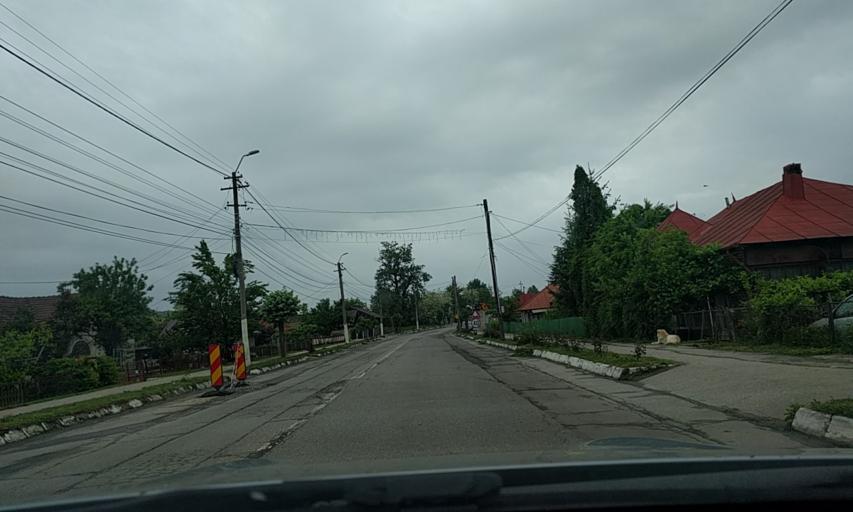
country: RO
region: Dambovita
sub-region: Oras Pucioasa
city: Glodeni
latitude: 45.0481
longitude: 25.4375
